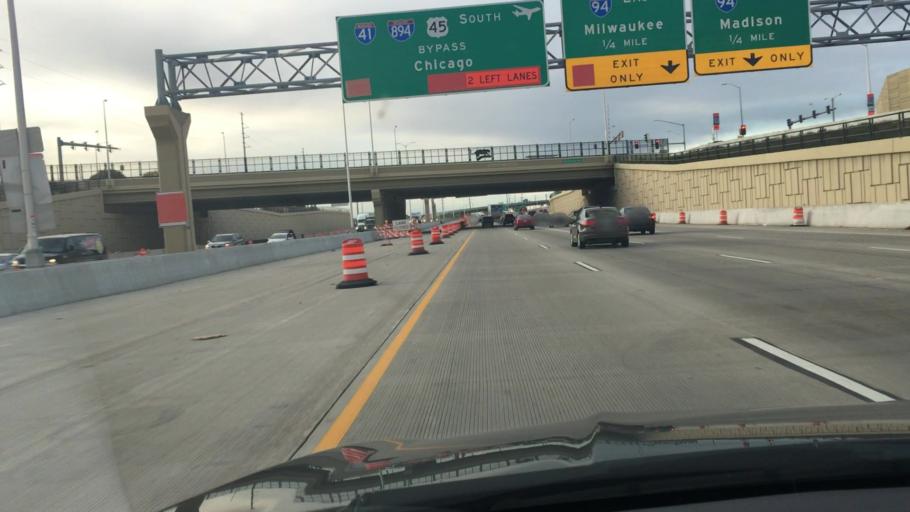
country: US
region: Wisconsin
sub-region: Milwaukee County
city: Wauwatosa
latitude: 43.0364
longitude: -88.0334
